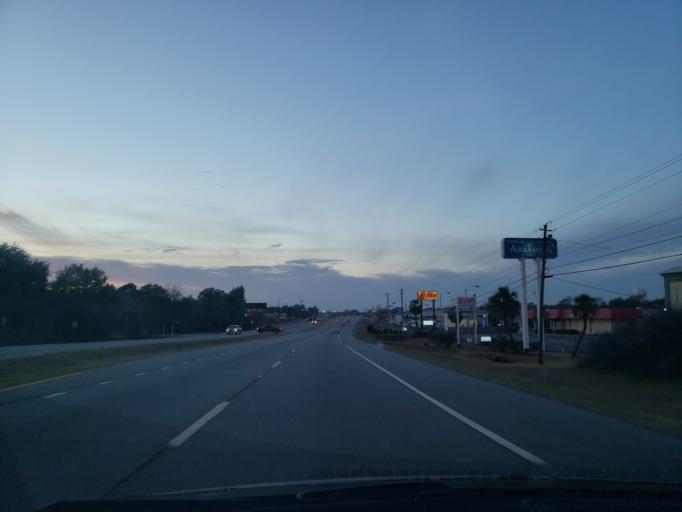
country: US
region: Georgia
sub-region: Dougherty County
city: Albany
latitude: 31.5727
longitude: -84.1282
